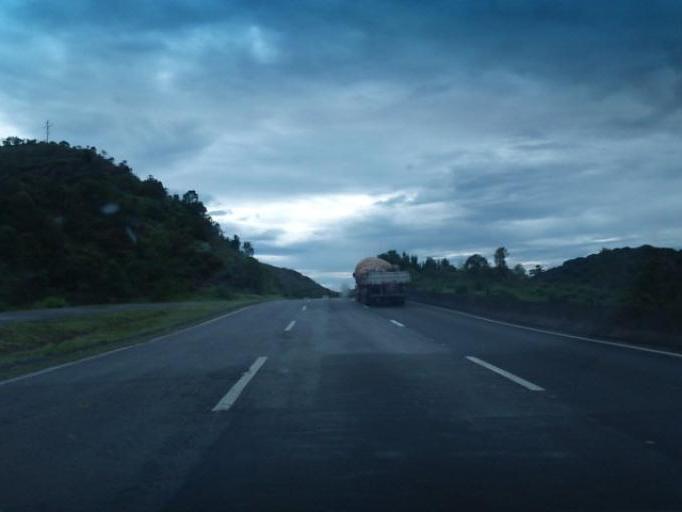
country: BR
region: Sao Paulo
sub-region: Cajati
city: Cajati
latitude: -24.9489
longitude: -48.4356
